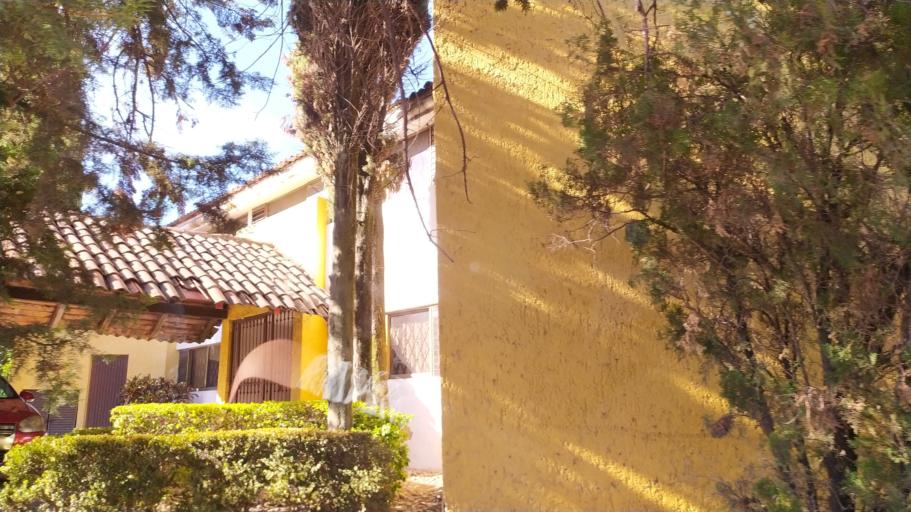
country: MX
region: Jalisco
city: Guadalajara
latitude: 20.6585
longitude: -103.4264
